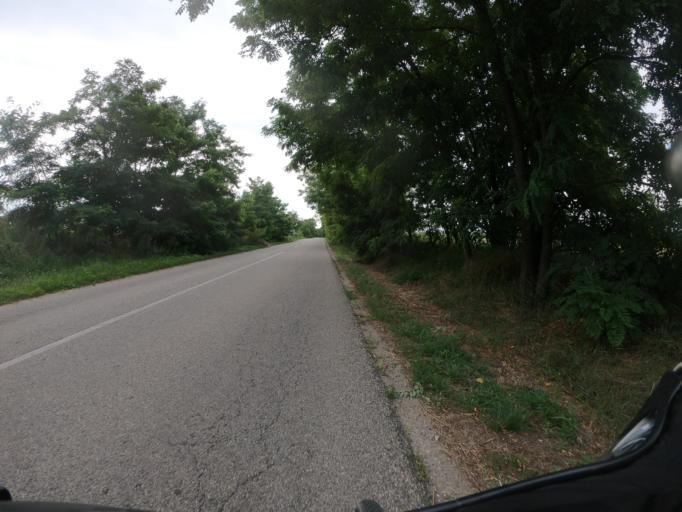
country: HU
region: Borsod-Abauj-Zemplen
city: Mezocsat
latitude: 47.8094
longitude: 20.9577
